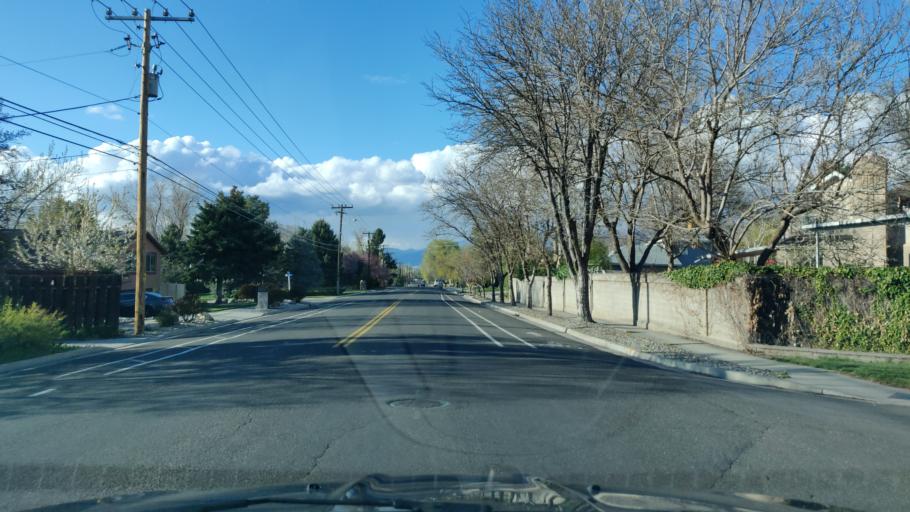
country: US
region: Utah
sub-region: Salt Lake County
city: Cottonwood Heights
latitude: 40.6301
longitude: -111.8247
